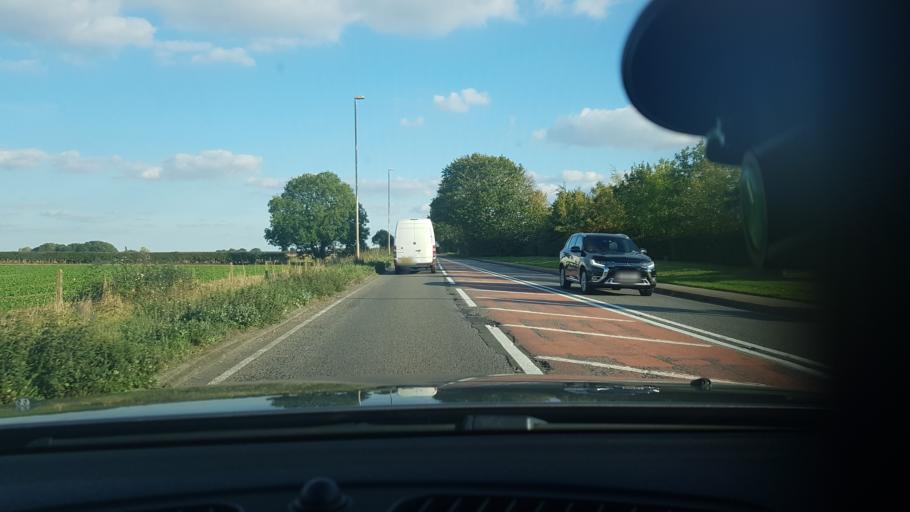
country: GB
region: England
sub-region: Gloucestershire
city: Cirencester
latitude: 51.7008
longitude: -1.9385
